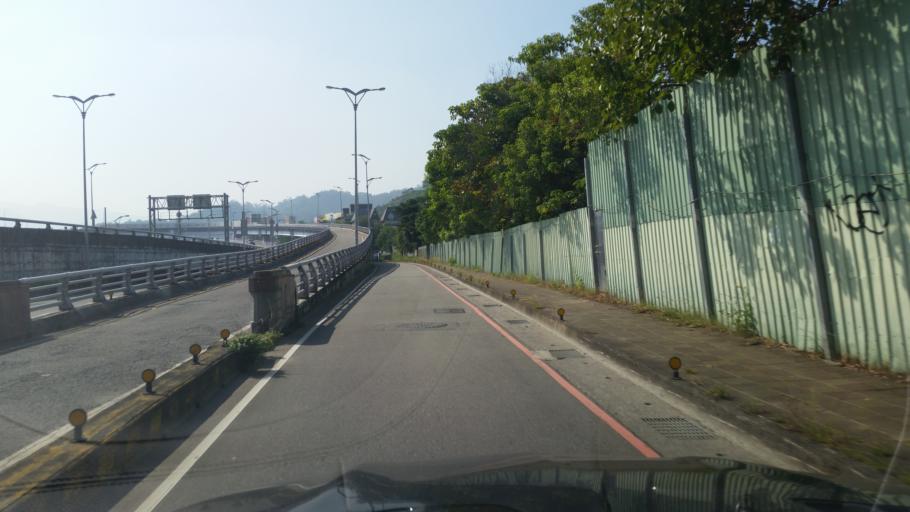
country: TW
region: Taipei
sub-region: Taipei
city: Banqiao
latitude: 24.9840
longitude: 121.5206
